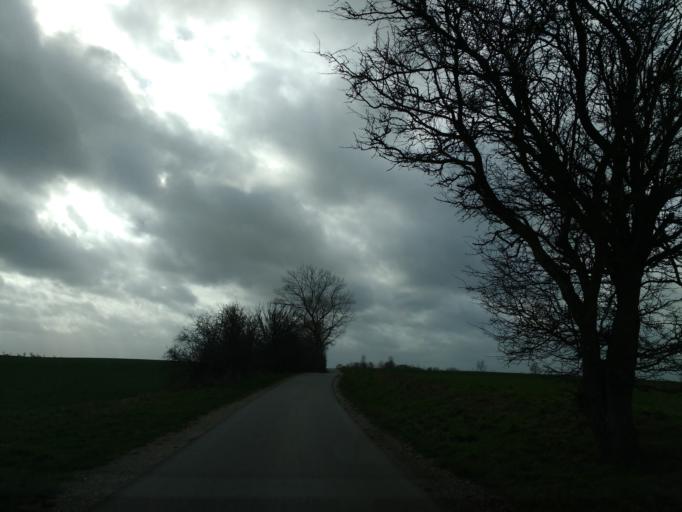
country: DE
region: Schleswig-Holstein
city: Heiligenhafen
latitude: 54.3690
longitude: 10.9489
